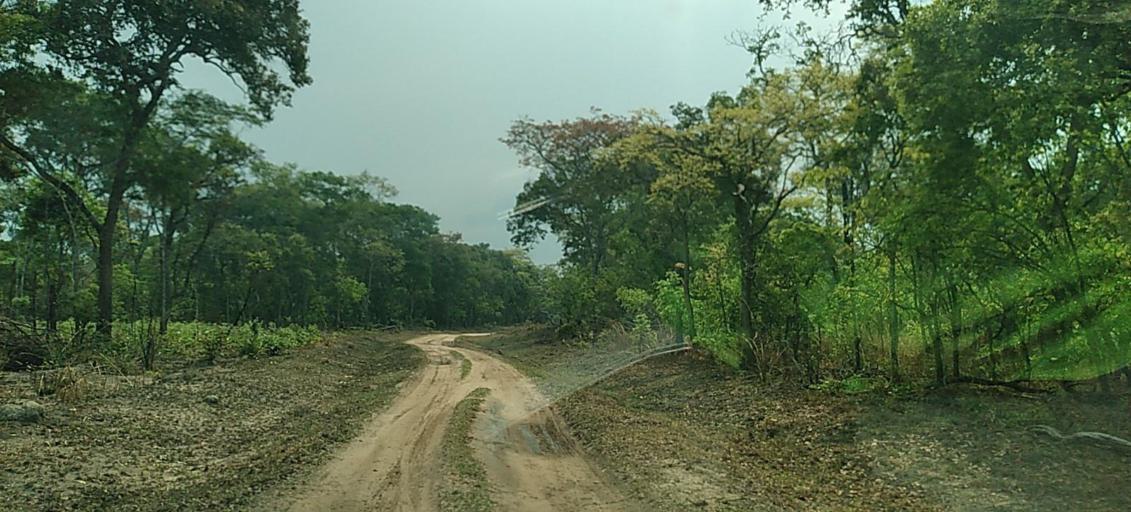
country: ZM
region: North-Western
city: Mwinilunga
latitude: -11.4702
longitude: 24.4851
